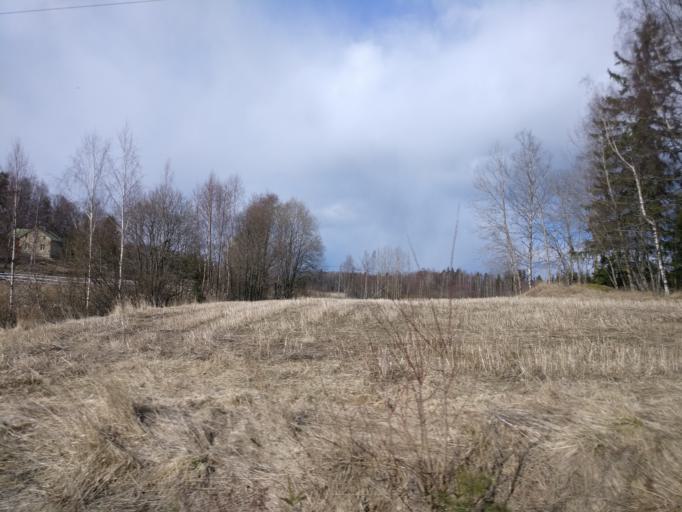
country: FI
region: Uusimaa
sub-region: Helsinki
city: Karjalohja
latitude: 60.3125
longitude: 23.7417
